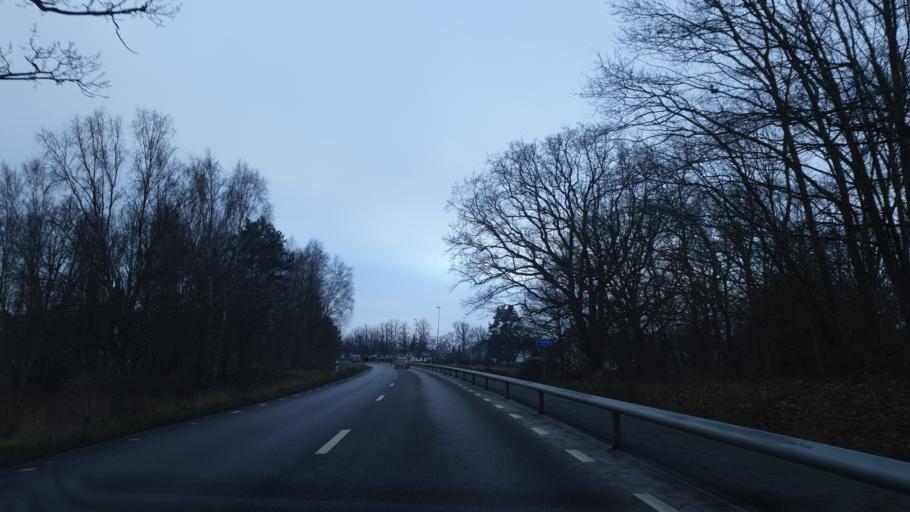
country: SE
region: Blekinge
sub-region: Solvesborgs Kommun
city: Soelvesborg
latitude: 56.0921
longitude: 14.6527
